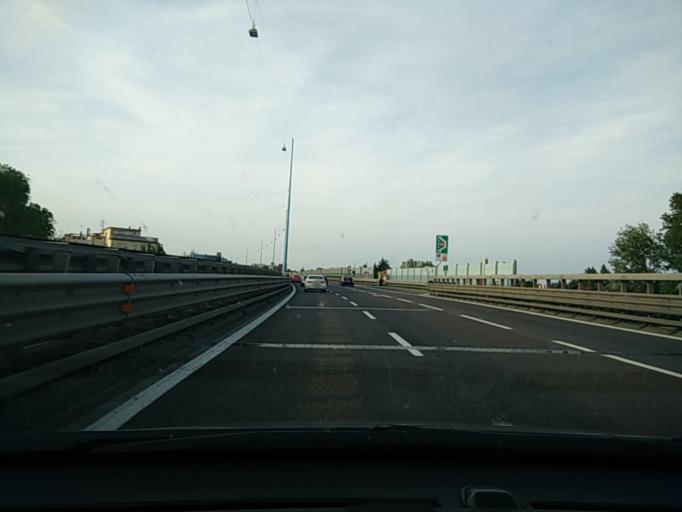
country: IT
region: Veneto
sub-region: Provincia di Venezia
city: Mestre
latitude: 45.4969
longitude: 12.2291
